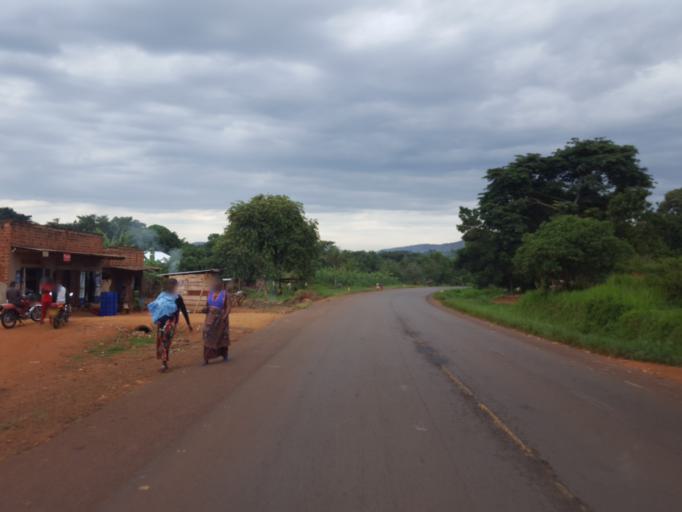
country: UG
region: Central Region
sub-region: Kiboga District
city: Kiboga
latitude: 0.8724
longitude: 31.8533
